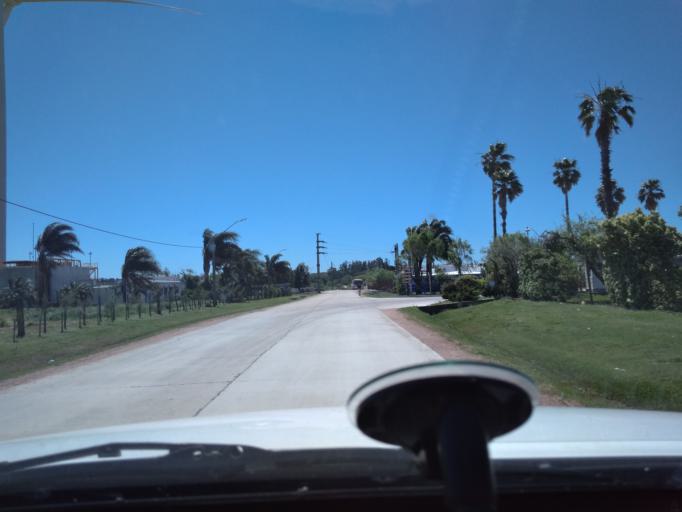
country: UY
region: Canelones
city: Progreso
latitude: -34.6882
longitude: -56.2975
